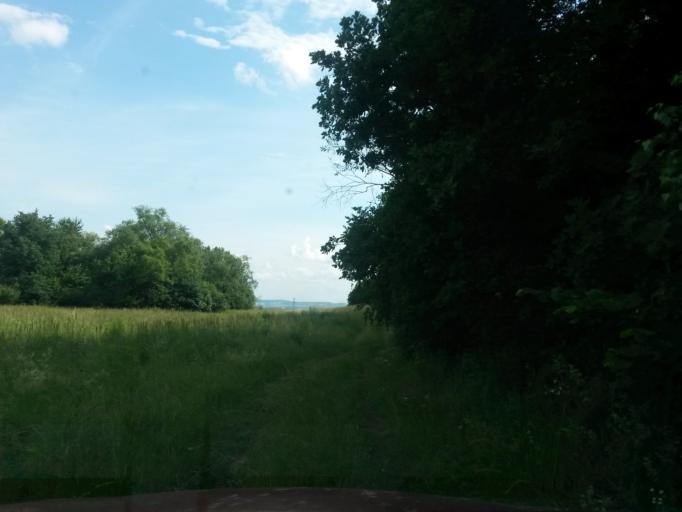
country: SK
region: Kosicky
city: Moldava nad Bodvou
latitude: 48.6217
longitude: 21.0989
